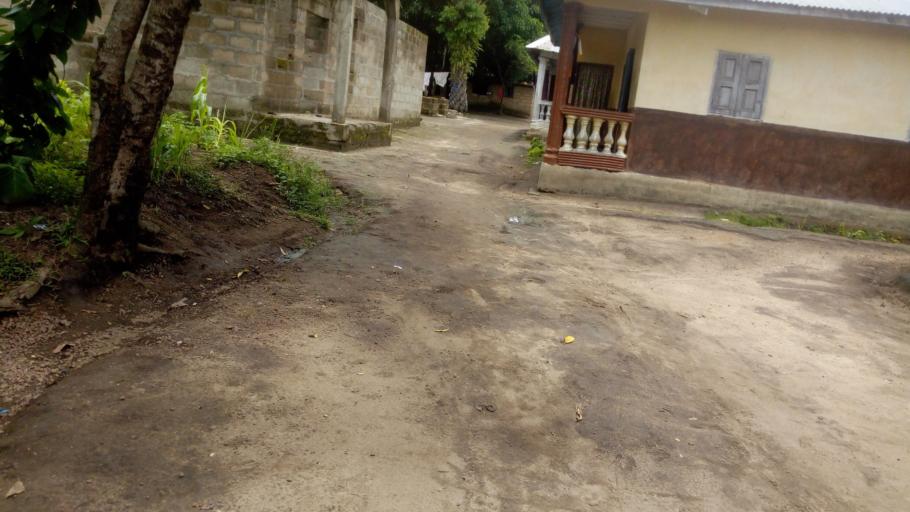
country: SL
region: Northern Province
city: Magburaka
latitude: 8.7157
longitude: -11.9550
